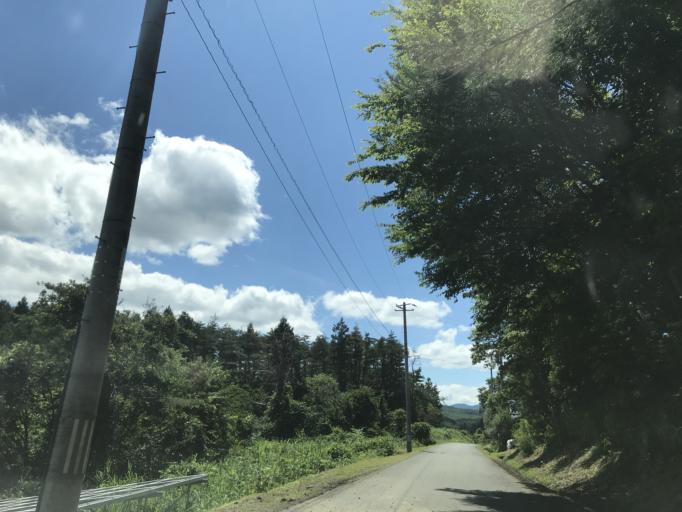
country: JP
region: Iwate
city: Ichinoseki
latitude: 38.9357
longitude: 141.0247
